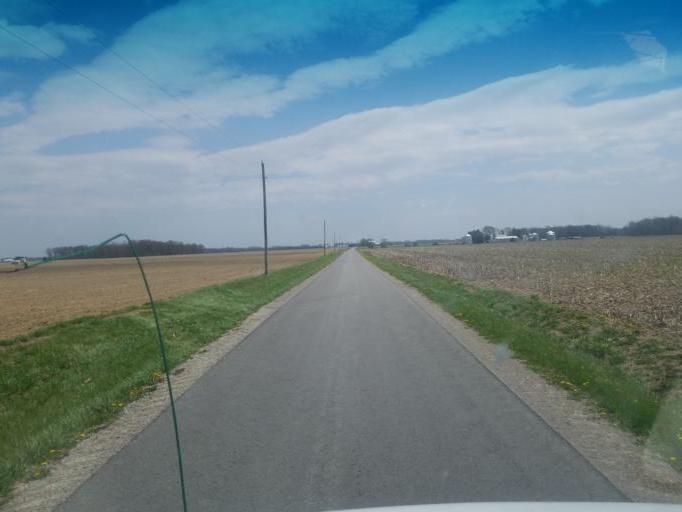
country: US
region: Ohio
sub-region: Hardin County
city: Forest
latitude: 40.7736
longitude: -83.3985
